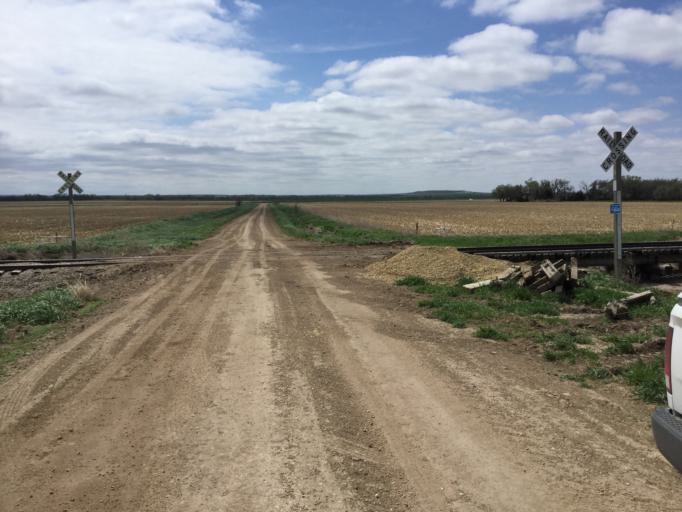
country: US
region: Kansas
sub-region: Osborne County
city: Osborne
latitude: 39.4424
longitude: -98.6759
